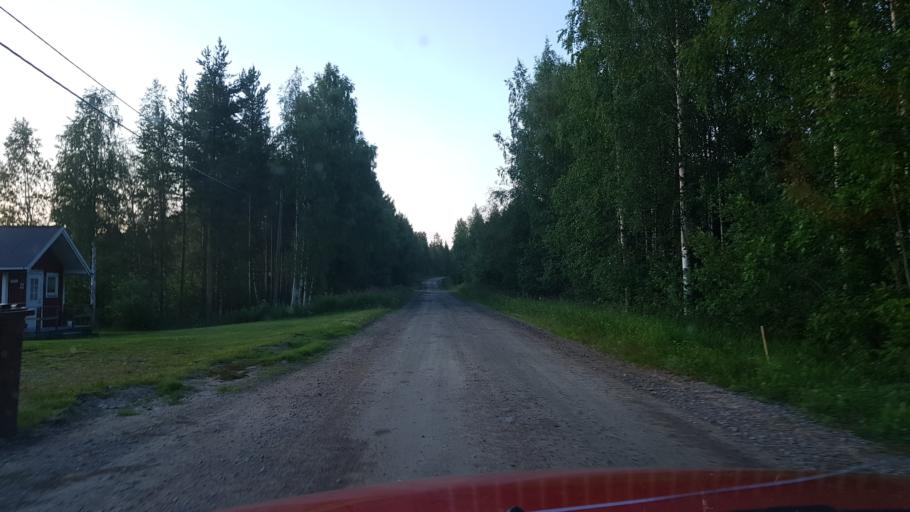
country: SE
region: Norrbotten
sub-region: Alvsbyns Kommun
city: AElvsbyn
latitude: 65.7015
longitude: 20.6814
